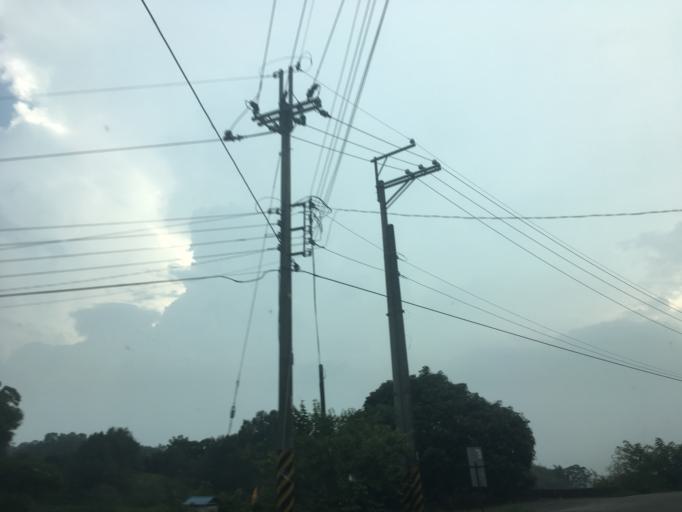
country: TW
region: Taiwan
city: Fengyuan
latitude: 24.1893
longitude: 120.7778
